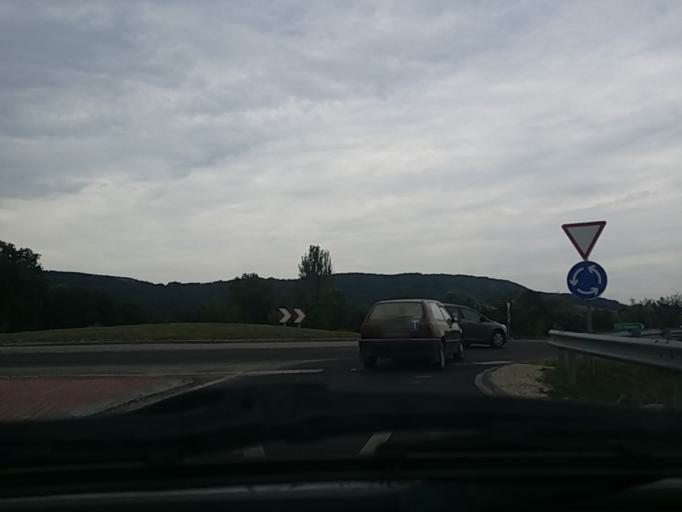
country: HU
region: Pest
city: Pilisborosjeno
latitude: 47.5976
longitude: 18.9656
